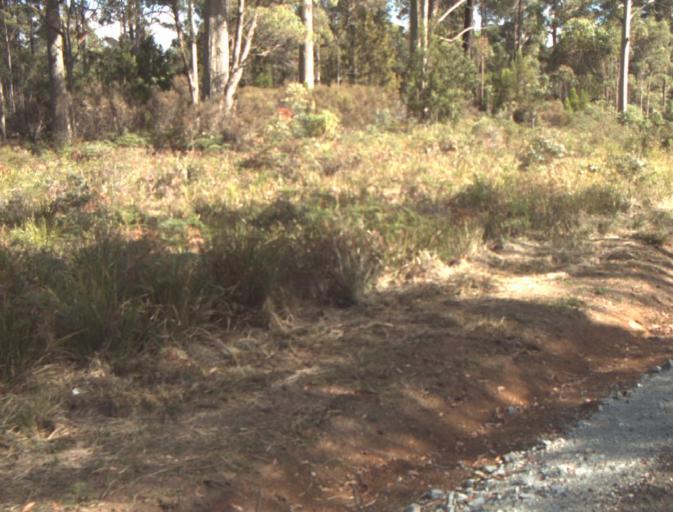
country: AU
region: Tasmania
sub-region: Launceston
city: Mayfield
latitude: -41.3109
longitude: 147.1985
